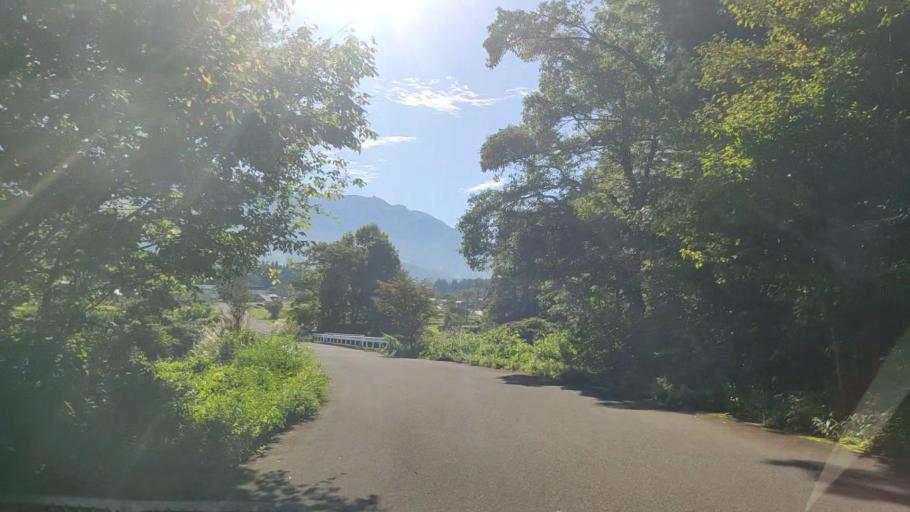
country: JP
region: Nagano
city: Iiyama
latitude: 36.8048
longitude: 138.4292
